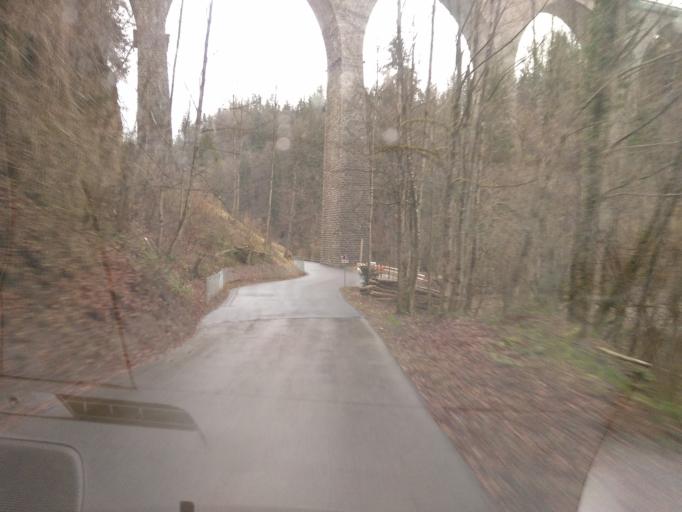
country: CH
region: Appenzell Ausserrhoden
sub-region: Bezirk Hinterland
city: Herisau
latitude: 47.4046
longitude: 9.3226
